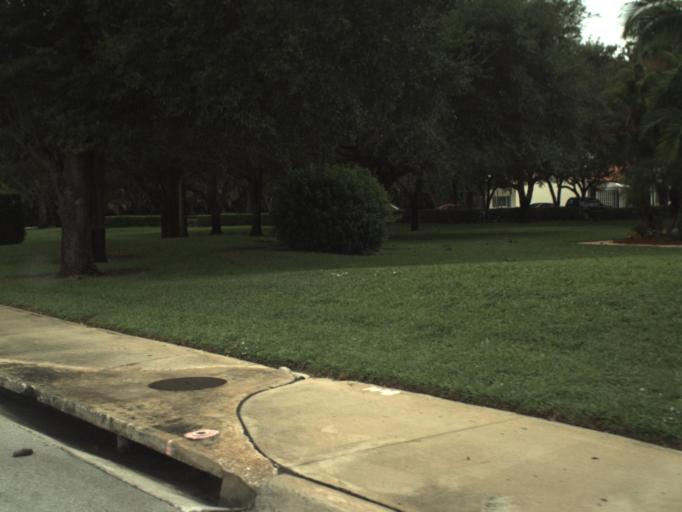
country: US
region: Florida
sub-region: Palm Beach County
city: North Palm Beach
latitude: 26.8230
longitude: -80.1059
